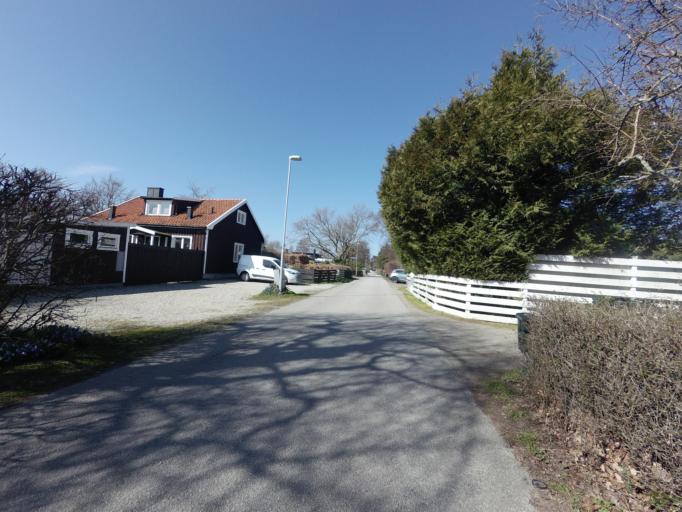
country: SE
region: Skane
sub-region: Vellinge Kommun
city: Skanor med Falsterbo
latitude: 55.3941
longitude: 12.8436
